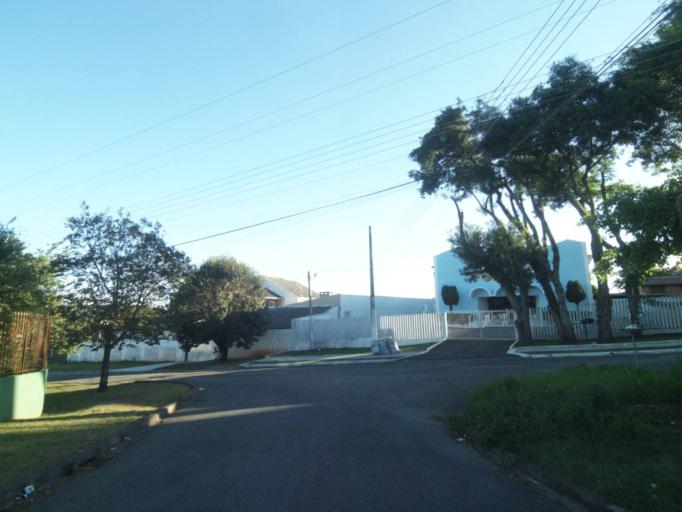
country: BR
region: Parana
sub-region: Curitiba
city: Curitiba
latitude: -25.3909
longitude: -49.2513
